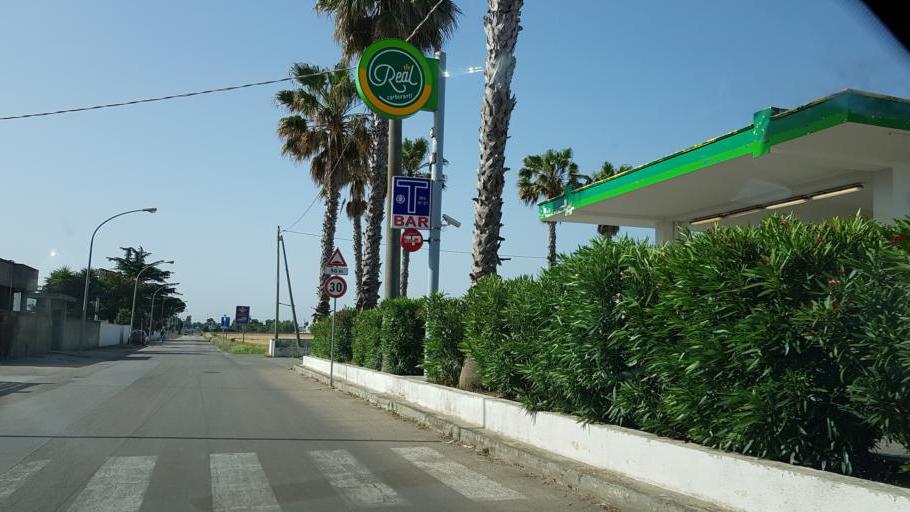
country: IT
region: Apulia
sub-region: Provincia di Brindisi
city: Mesagne
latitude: 40.5488
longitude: 17.8132
